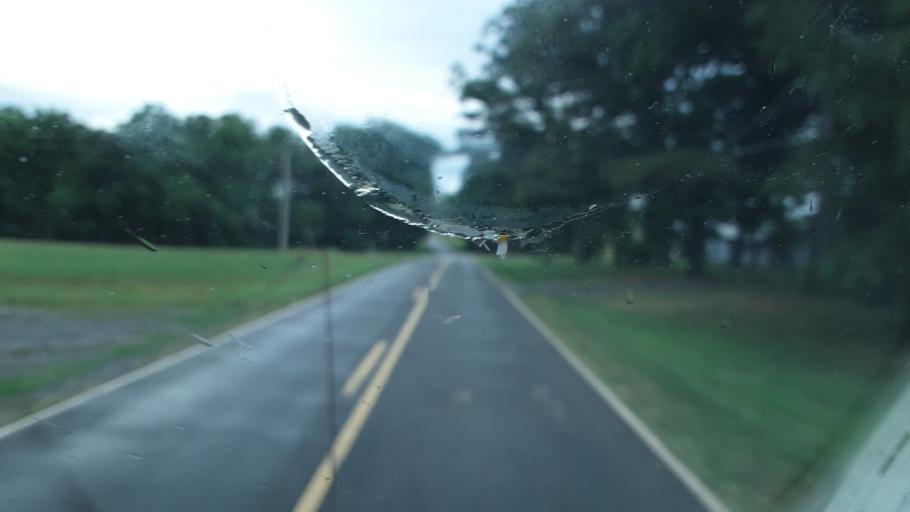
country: US
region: North Carolina
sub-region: Yadkin County
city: Yadkinville
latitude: 36.0538
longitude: -80.8273
